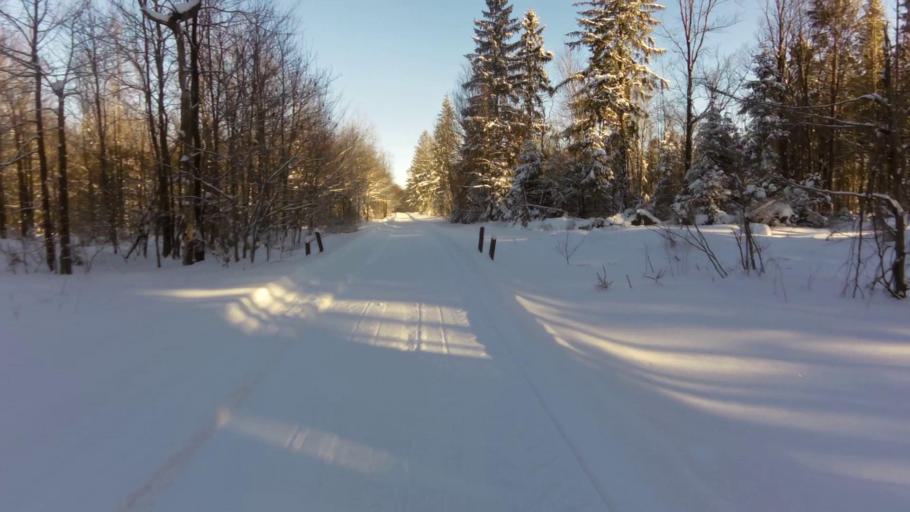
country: US
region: New York
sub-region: Chautauqua County
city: Falconer
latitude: 42.2446
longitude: -79.2131
